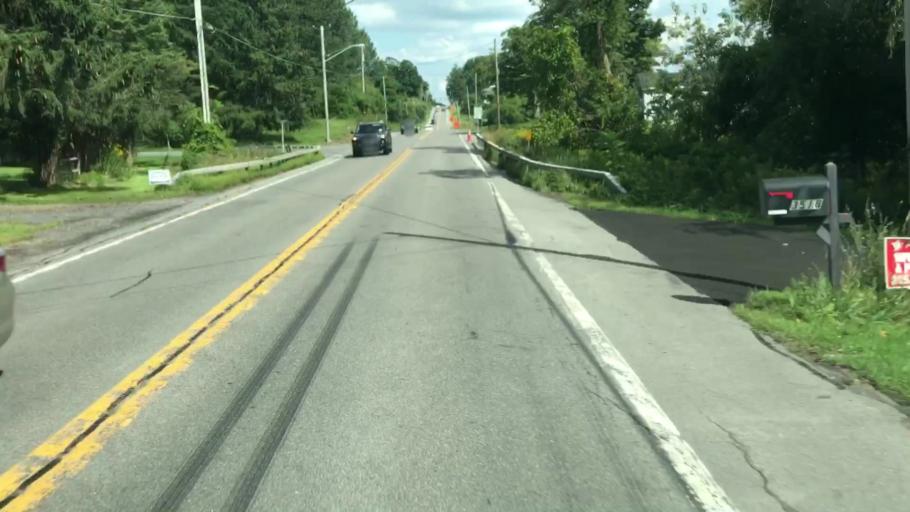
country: US
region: New York
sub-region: Onondaga County
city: Camillus
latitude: 42.9848
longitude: -76.2671
